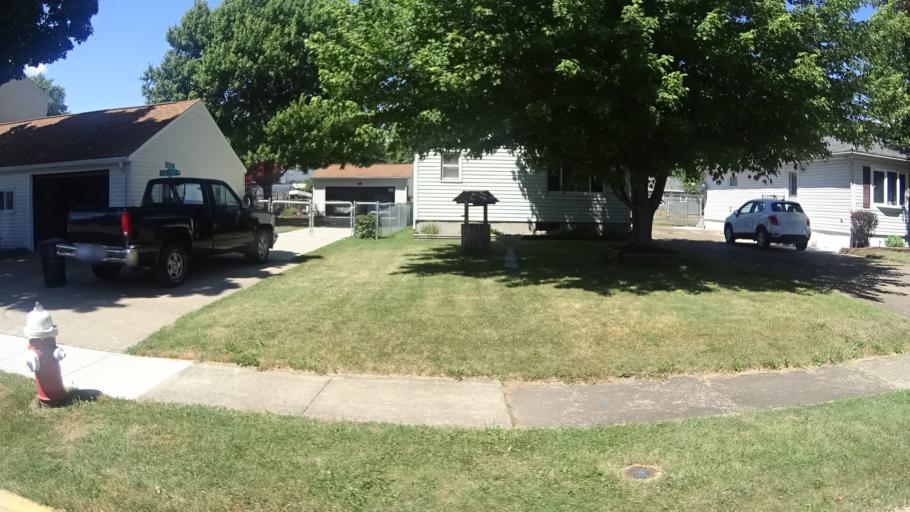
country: US
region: Ohio
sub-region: Erie County
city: Sandusky
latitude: 41.4350
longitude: -82.7354
